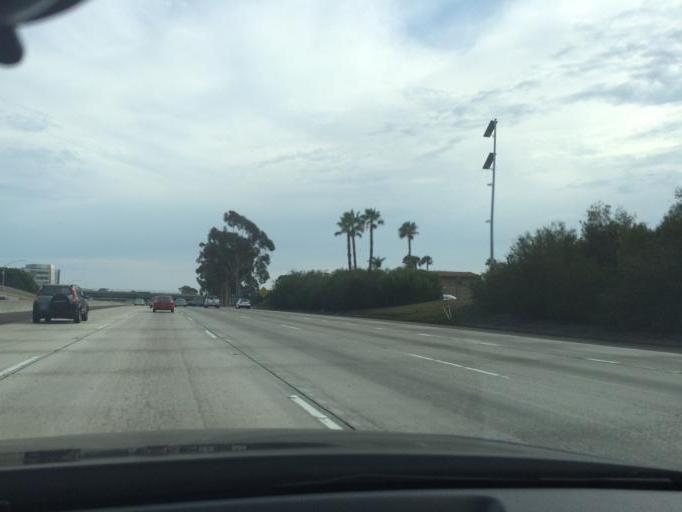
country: US
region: California
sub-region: San Diego County
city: San Diego
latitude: 32.8052
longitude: -117.1543
